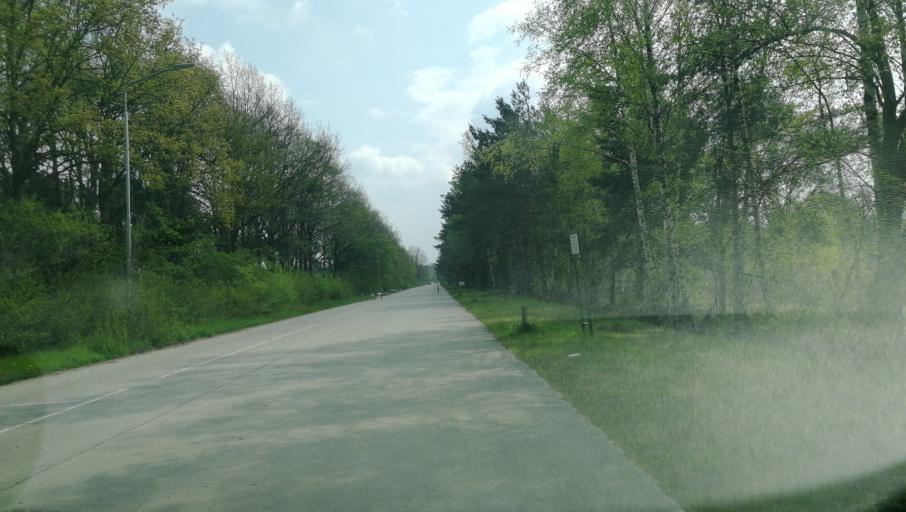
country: NL
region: Limburg
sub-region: Gemeente Venlo
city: Venlo
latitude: 51.3751
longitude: 6.2084
